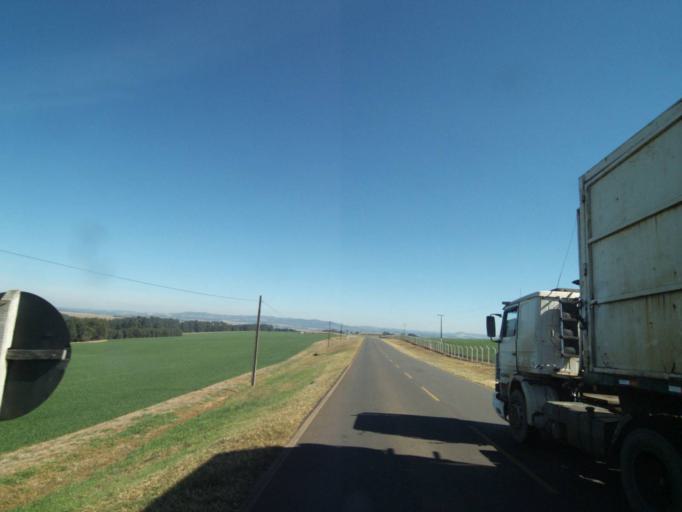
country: BR
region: Parana
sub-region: Tibagi
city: Tibagi
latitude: -24.5231
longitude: -50.3597
